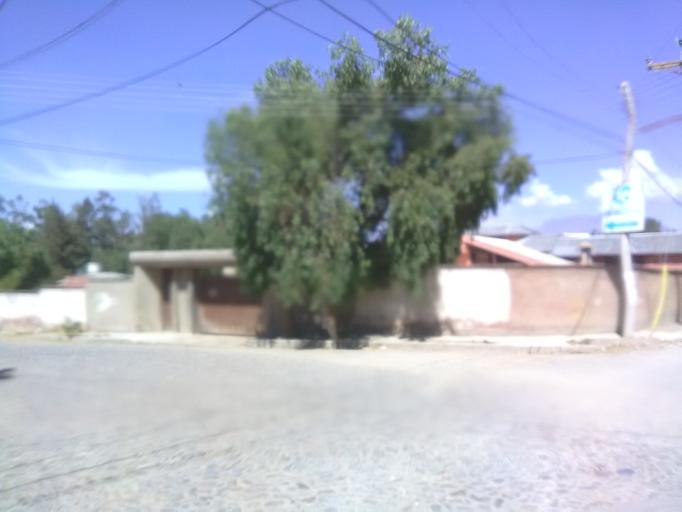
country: BO
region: Cochabamba
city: Cochabamba
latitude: -17.3527
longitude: -66.2006
